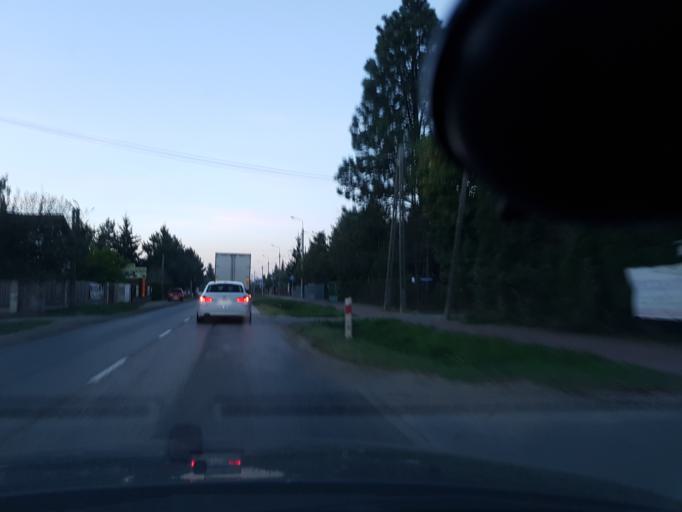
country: PL
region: Masovian Voivodeship
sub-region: Powiat grodziski
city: Grodzisk Mazowiecki
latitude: 52.0851
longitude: 20.6115
